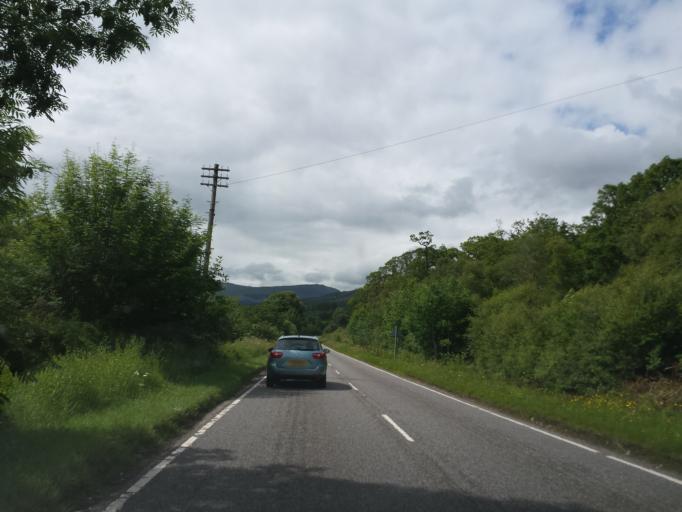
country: GB
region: Scotland
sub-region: Highland
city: Fort William
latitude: 56.8496
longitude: -5.1662
